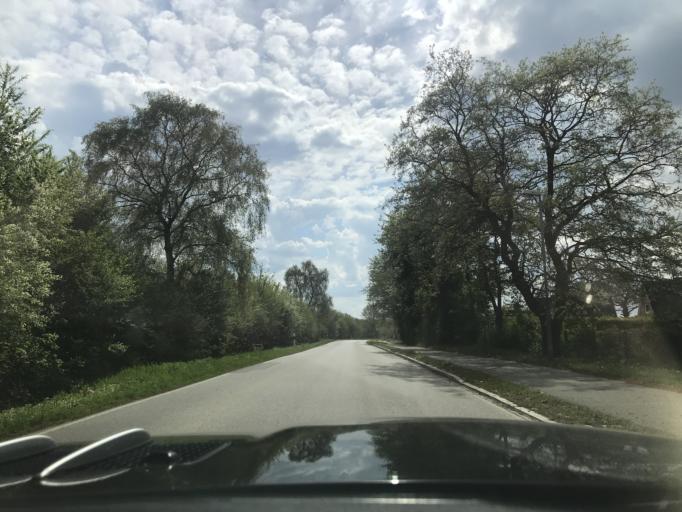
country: DE
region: Schleswig-Holstein
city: Timmendorfer Strand
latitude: 53.9613
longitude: 10.8152
